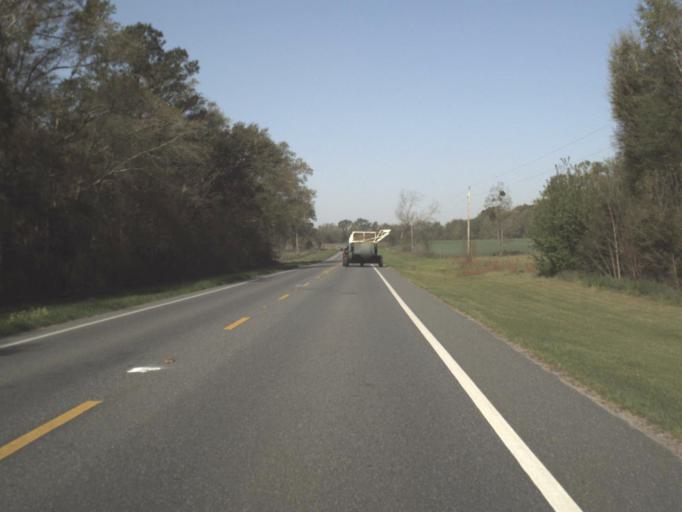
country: US
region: Florida
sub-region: Jackson County
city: Malone
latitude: 30.9601
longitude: -85.2028
